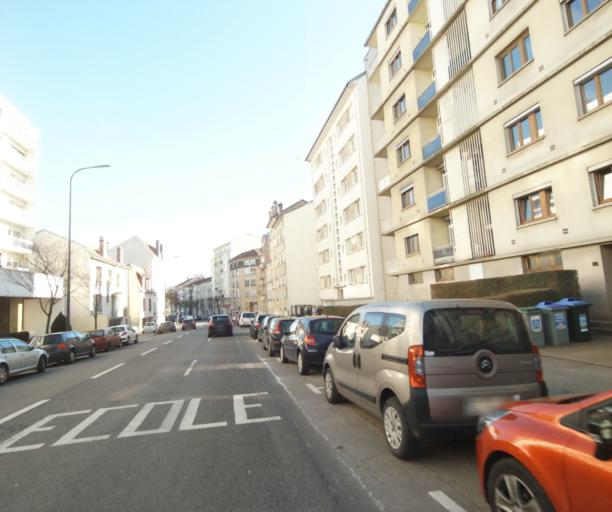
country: FR
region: Lorraine
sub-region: Departement de Meurthe-et-Moselle
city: Nancy
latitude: 48.6755
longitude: 6.1797
